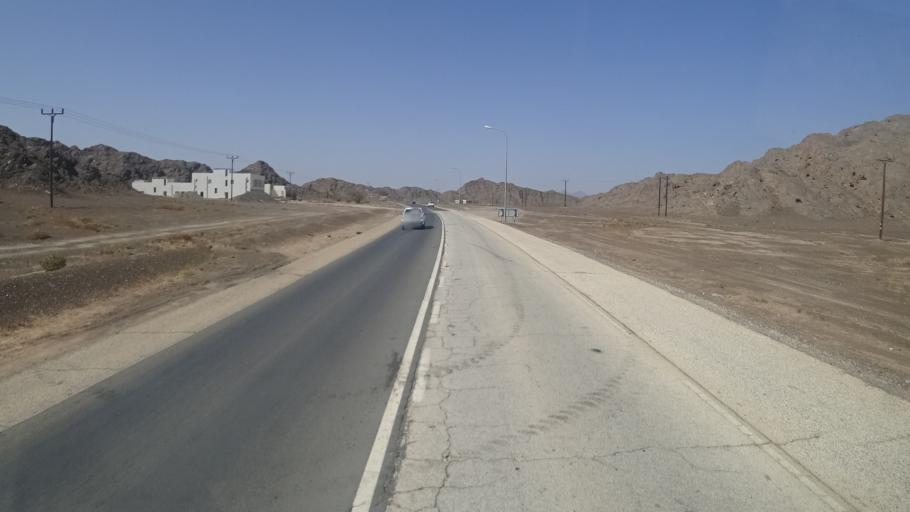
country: OM
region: Ash Sharqiyah
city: Ibra'
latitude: 22.6862
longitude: 58.5756
